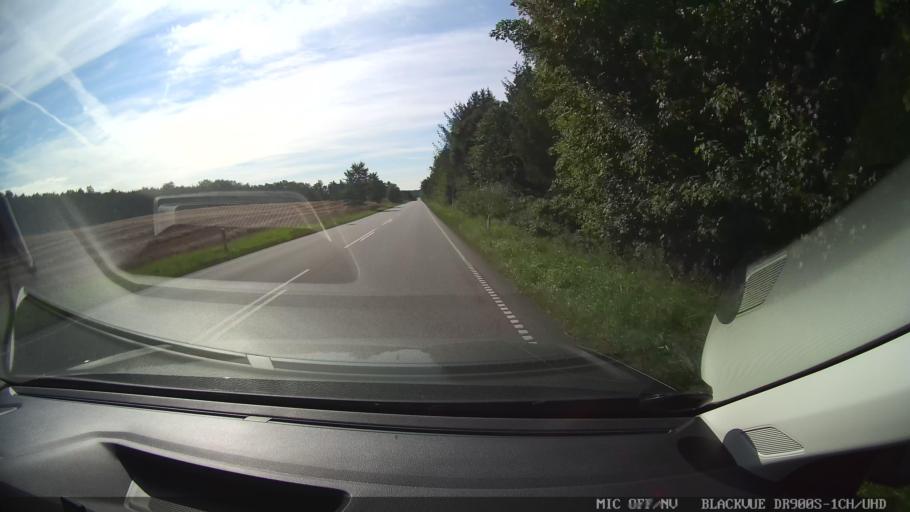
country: DK
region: North Denmark
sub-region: Mariagerfjord Kommune
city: Hadsund
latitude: 56.7492
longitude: 10.0735
